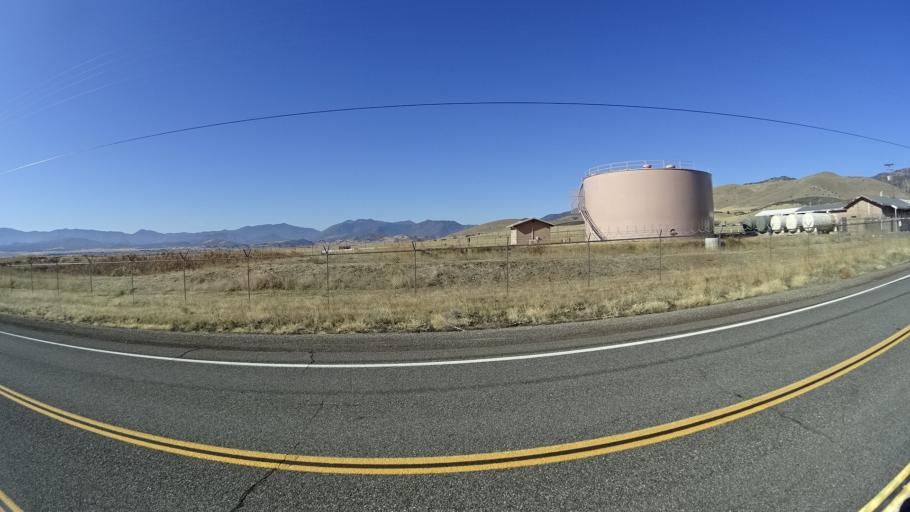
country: US
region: California
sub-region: Siskiyou County
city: Montague
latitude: 41.7707
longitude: -122.5247
